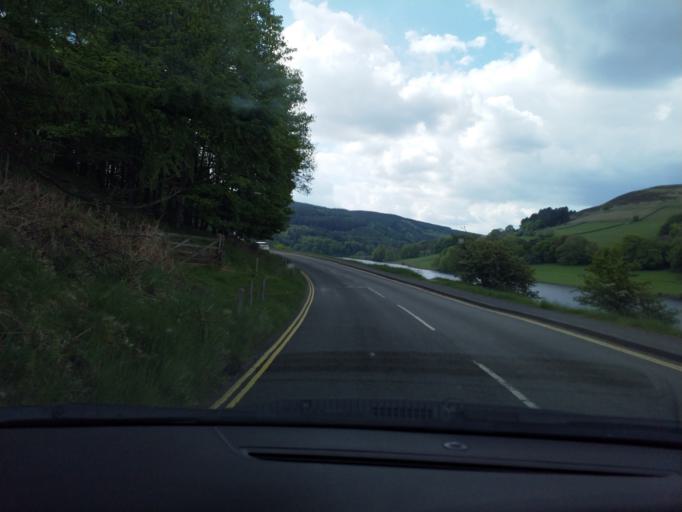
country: GB
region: England
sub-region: Derbyshire
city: Hope Valley
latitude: 53.3922
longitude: -1.7274
